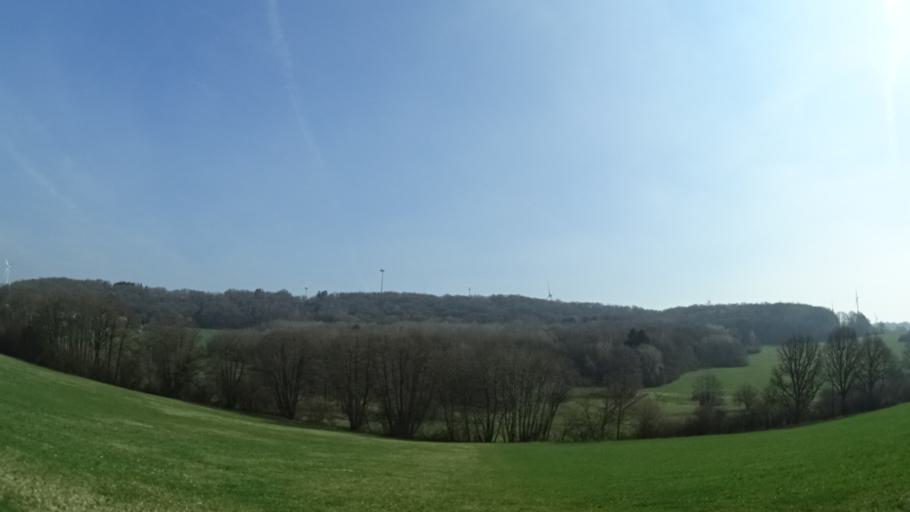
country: DE
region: Rheinland-Pfalz
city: Gimbweiler
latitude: 49.5774
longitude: 7.1846
